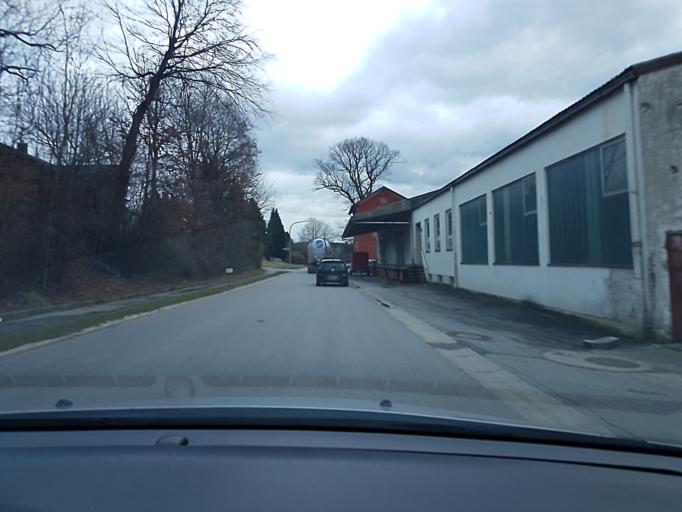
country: DE
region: Bavaria
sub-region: Upper Bavaria
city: Egglkofen
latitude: 48.3963
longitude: 12.4450
